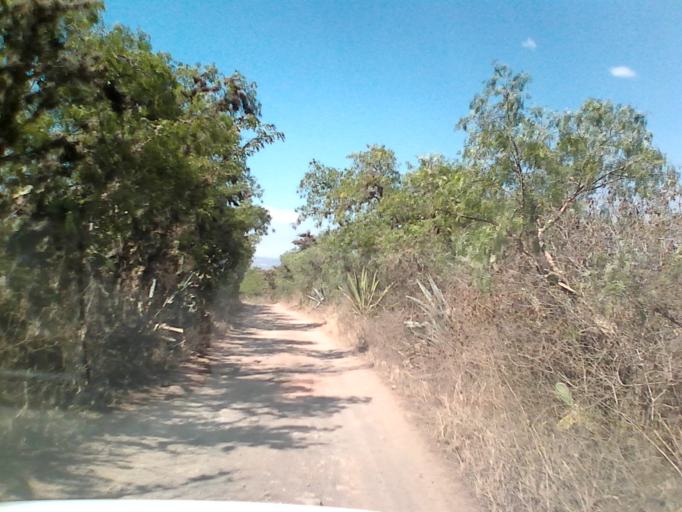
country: CO
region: Boyaca
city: Sachica
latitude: 5.6072
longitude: -73.5573
